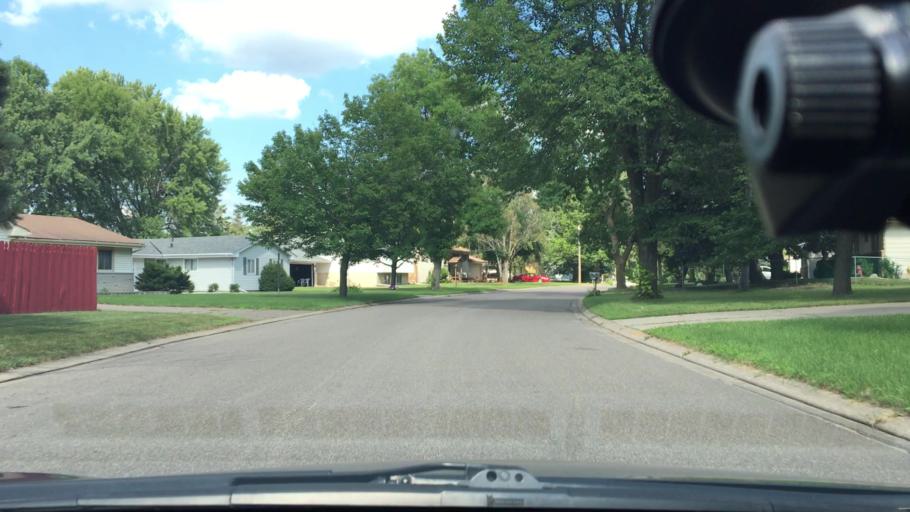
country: US
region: Minnesota
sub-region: Hennepin County
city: New Hope
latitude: 45.0377
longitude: -93.3889
